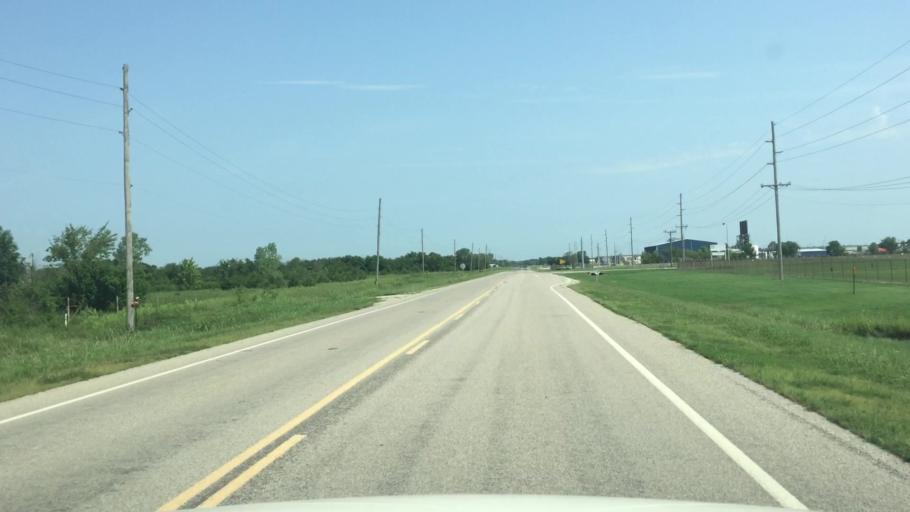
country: US
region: Kansas
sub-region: Montgomery County
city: Coffeyville
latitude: 37.0878
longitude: -95.5863
